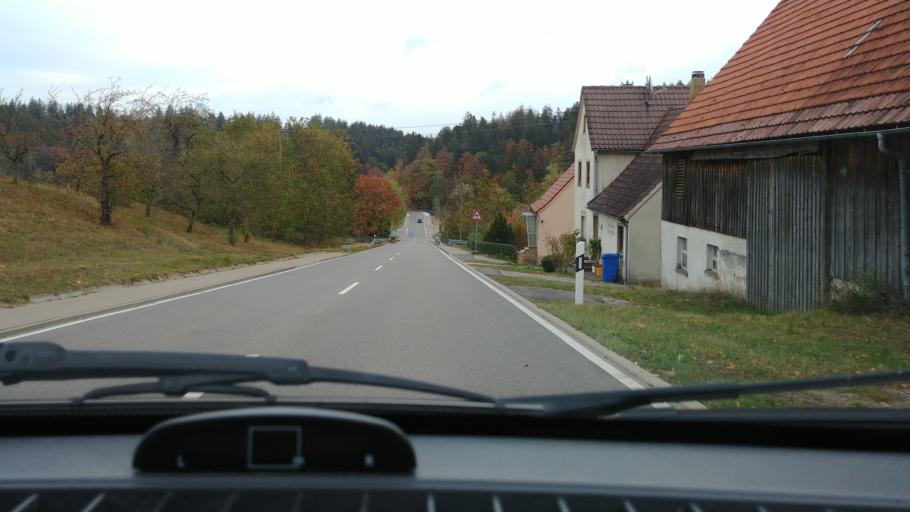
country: DE
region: Baden-Wuerttemberg
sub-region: Regierungsbezirk Stuttgart
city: Jagstzell
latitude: 49.0131
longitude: 10.1037
